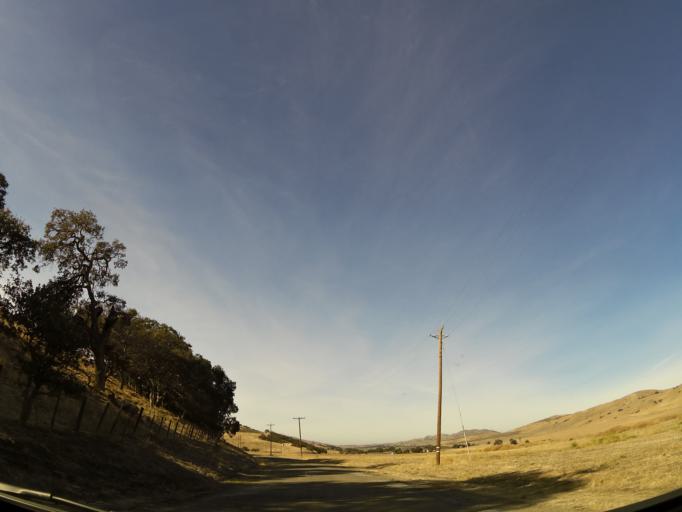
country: US
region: California
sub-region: San Benito County
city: Ridgemark
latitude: 36.6728
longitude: -121.2566
